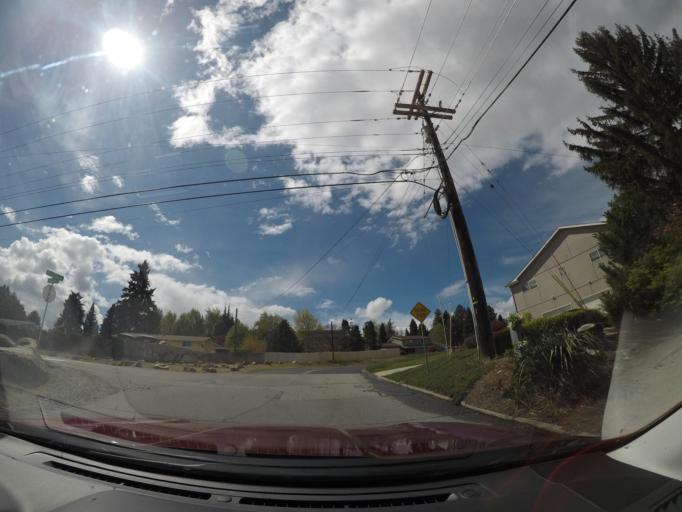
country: US
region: Washington
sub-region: Chelan County
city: West Wenatchee
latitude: 47.4552
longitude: -120.3412
